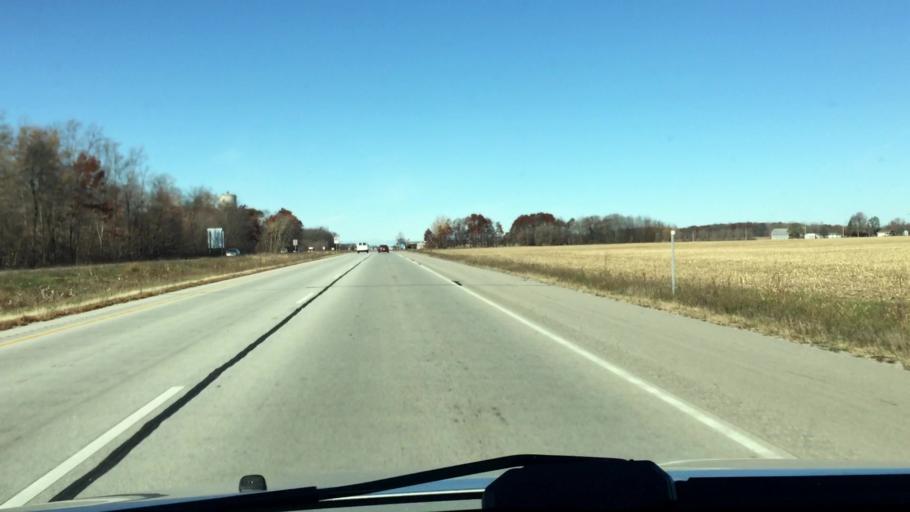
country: US
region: Wisconsin
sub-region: Brown County
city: Howard
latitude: 44.5687
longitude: -88.1505
